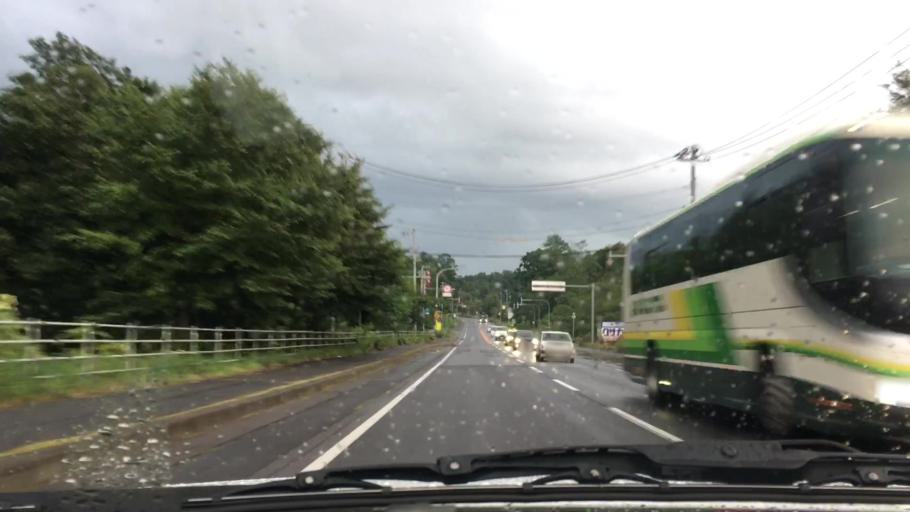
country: JP
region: Hokkaido
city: Nanae
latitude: 42.0858
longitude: 140.5843
